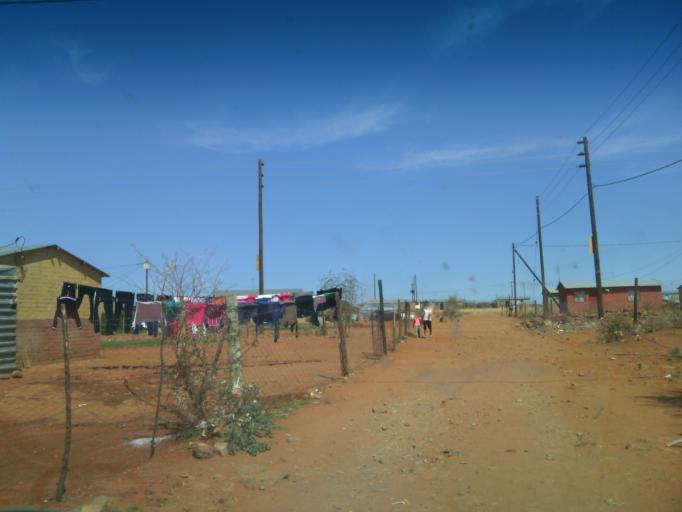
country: ZA
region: Northern Cape
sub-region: Frances Baard District Municipality
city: Barkly West
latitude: -28.5242
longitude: 24.5009
